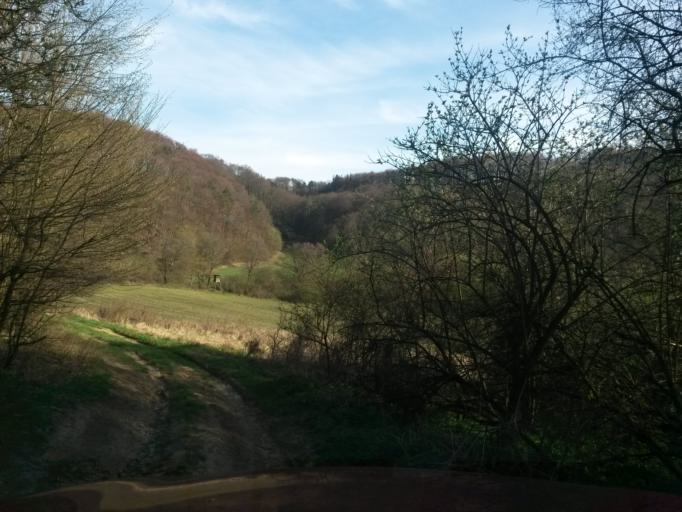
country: SK
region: Presovsky
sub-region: Okres Presov
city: Presov
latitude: 48.9047
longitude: 21.2085
